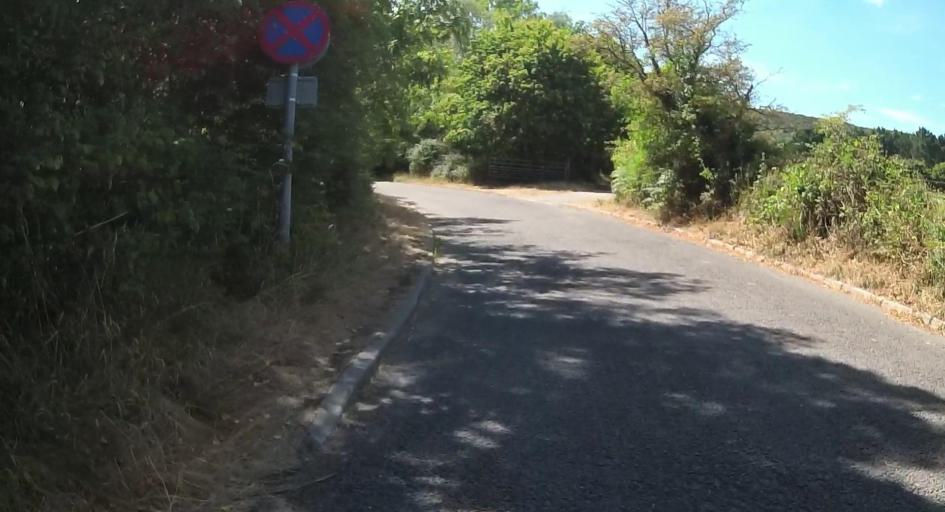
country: GB
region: England
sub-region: Dorset
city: Wareham
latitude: 50.6462
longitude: -2.0654
